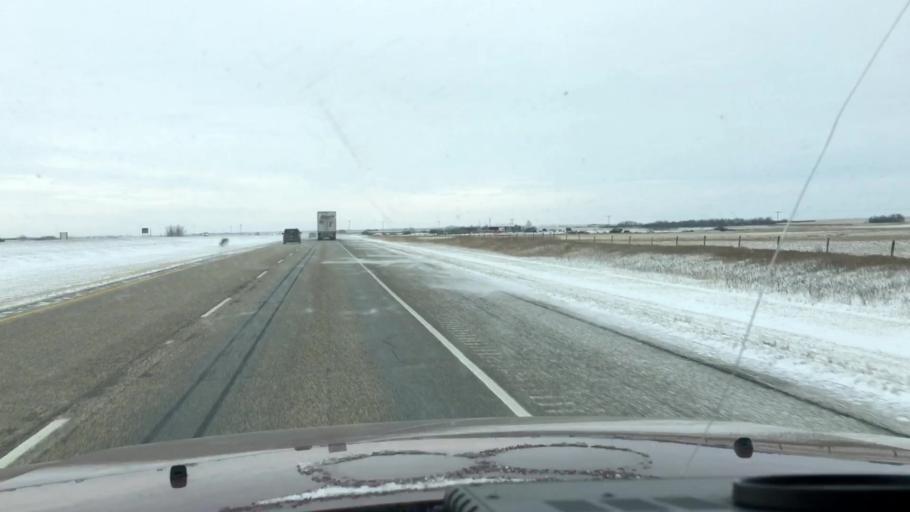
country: CA
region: Saskatchewan
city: Saskatoon
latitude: 51.6163
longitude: -106.4156
